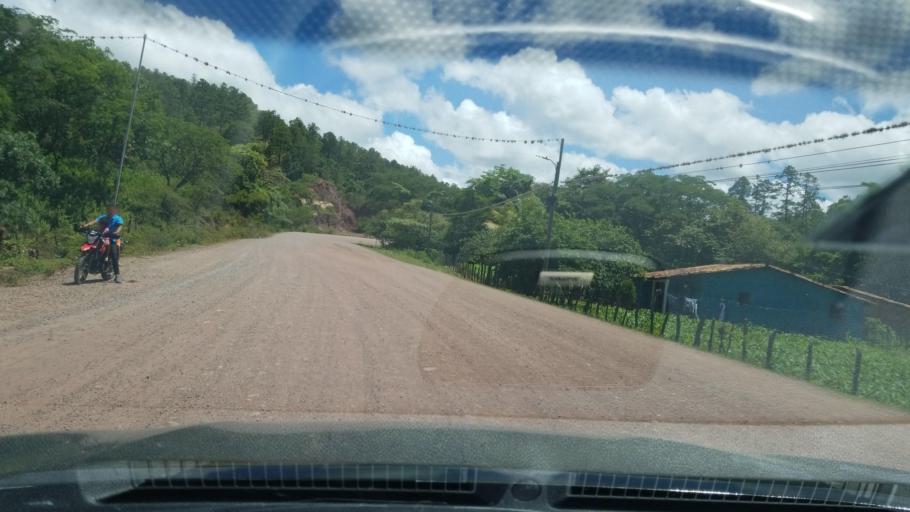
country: HN
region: Francisco Morazan
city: San Juan de Flores
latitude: 14.3391
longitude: -87.0429
